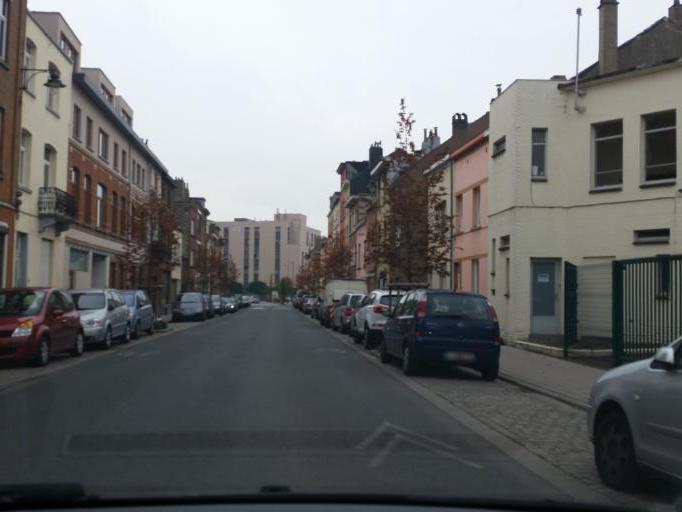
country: BE
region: Flanders
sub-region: Provincie Vlaams-Brabant
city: Drogenbos
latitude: 50.8131
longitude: 4.3190
